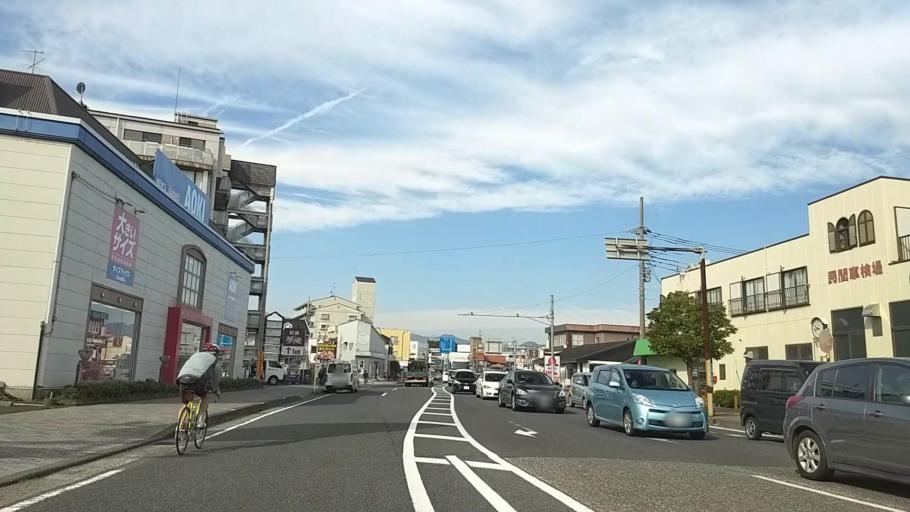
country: JP
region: Kanagawa
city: Atsugi
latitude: 35.4499
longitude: 139.3572
